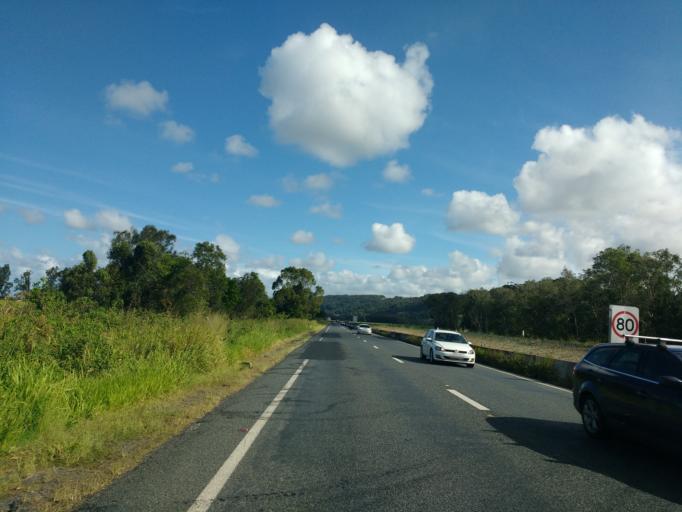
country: AU
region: New South Wales
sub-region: Ballina
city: Ballina
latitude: -28.8793
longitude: 153.4872
